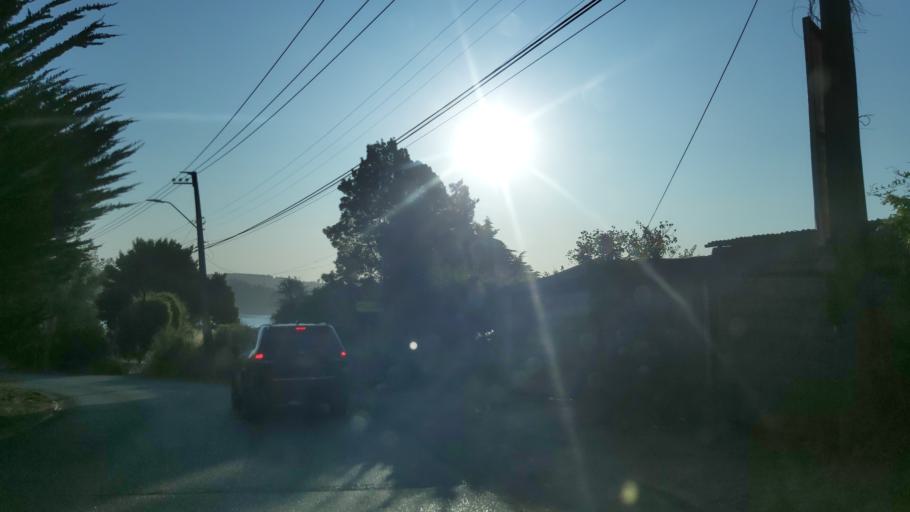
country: CL
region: Biobio
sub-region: Provincia de Concepcion
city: Tome
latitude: -36.5392
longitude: -72.9309
